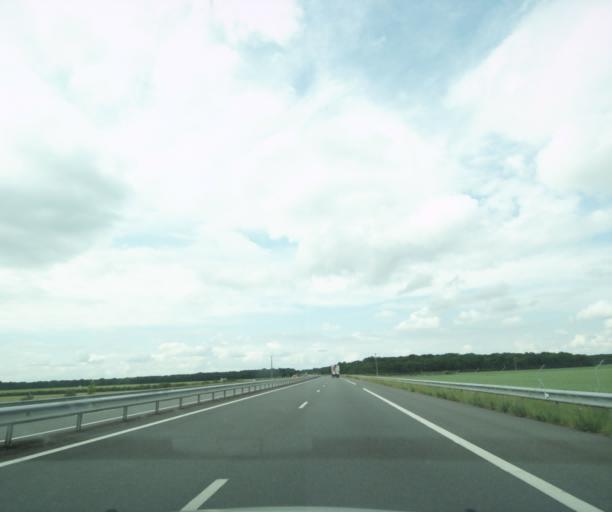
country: FR
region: Centre
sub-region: Departement du Cher
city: Levet
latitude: 46.8650
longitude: 2.4275
